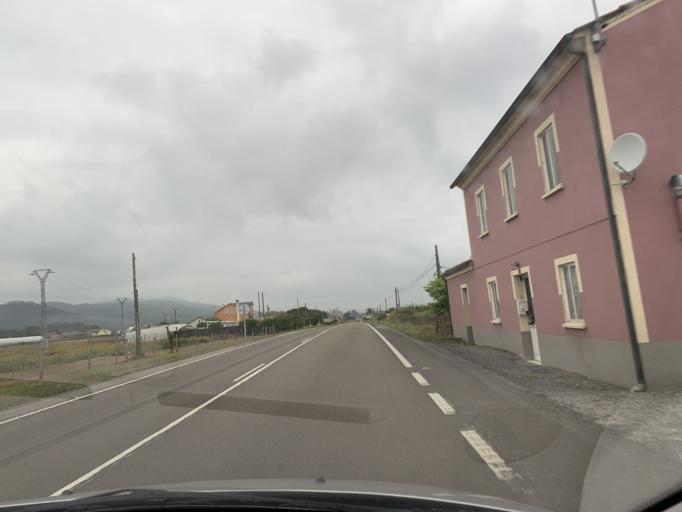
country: ES
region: Galicia
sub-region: Provincia de Lugo
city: Ribadeo
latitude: 43.5465
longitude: -7.0993
